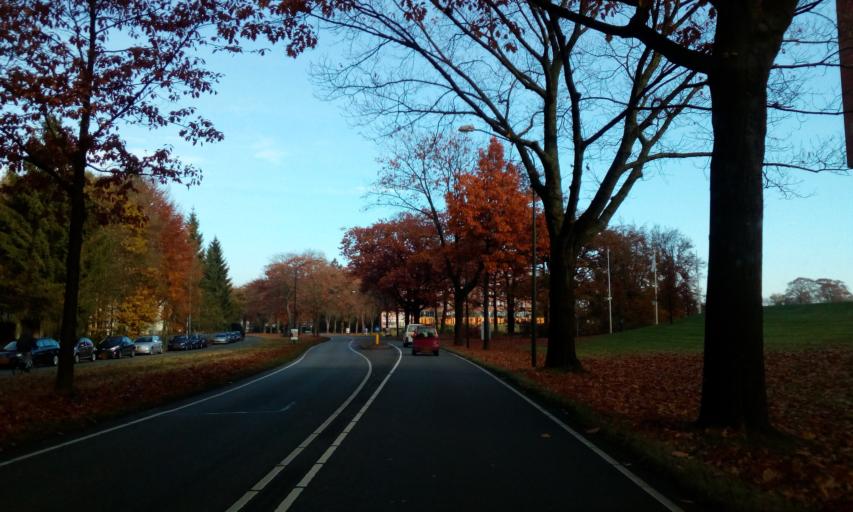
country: NL
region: Gelderland
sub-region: Gemeente Apeldoorn
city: Apeldoorn
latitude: 52.1964
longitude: 5.9445
